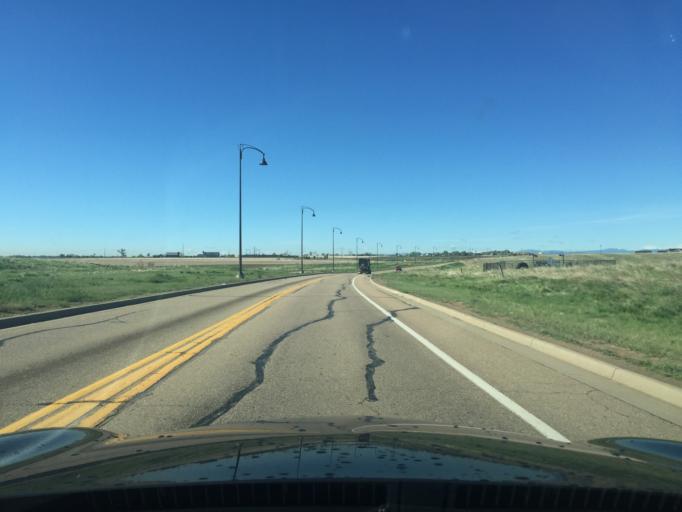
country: US
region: Colorado
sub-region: Boulder County
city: Erie
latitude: 39.9983
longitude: -105.0083
